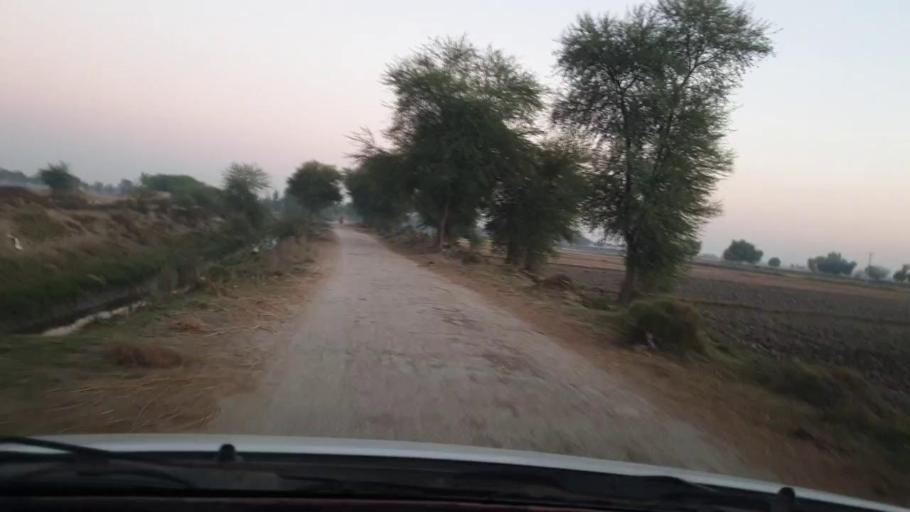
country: PK
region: Sindh
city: Khairpur Nathan Shah
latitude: 27.1491
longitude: 67.6965
